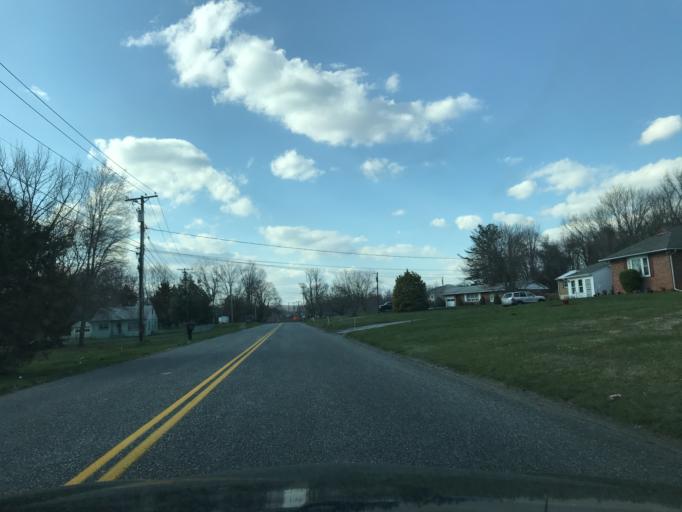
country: US
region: Maryland
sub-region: Harford County
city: Perryman
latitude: 39.4810
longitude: -76.2083
